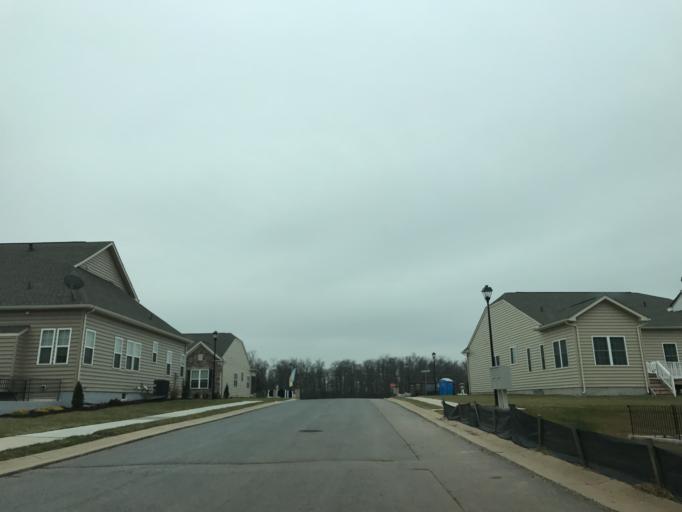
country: US
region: Maryland
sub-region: Carroll County
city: Taneytown
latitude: 39.6390
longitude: -77.1571
